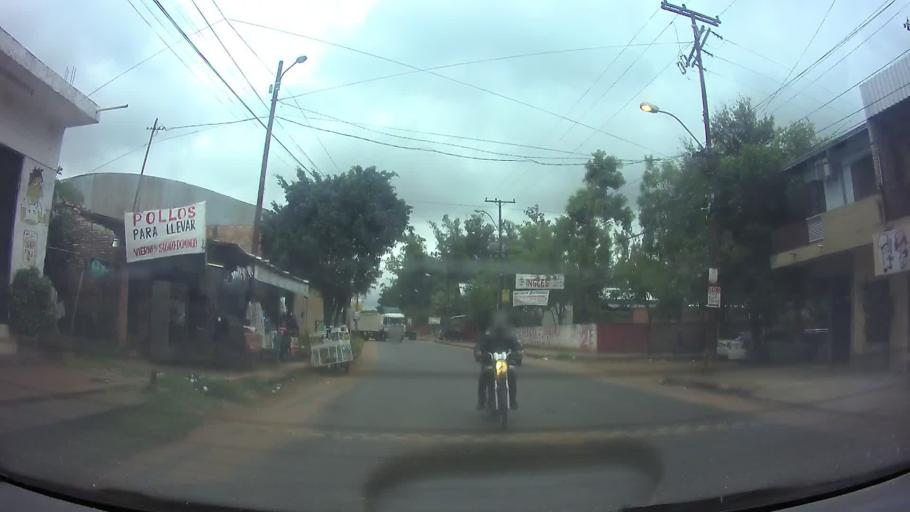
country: PY
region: Central
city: Nemby
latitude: -25.3842
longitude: -57.5479
